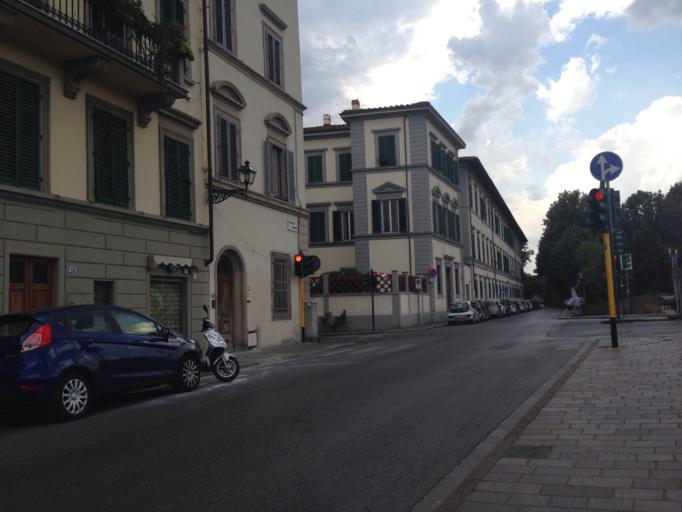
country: IT
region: Tuscany
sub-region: Province of Florence
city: Florence
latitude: 43.7712
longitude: 11.2426
